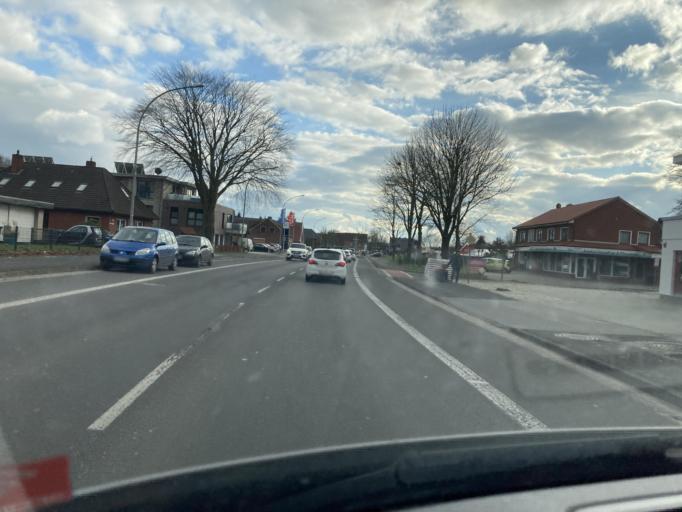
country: DE
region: Lower Saxony
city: Ostrhauderfehn
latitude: 53.1427
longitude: 7.5669
